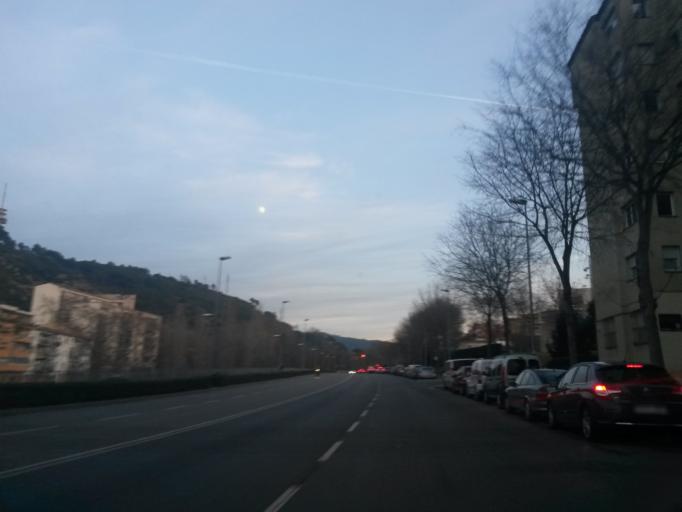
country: ES
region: Catalonia
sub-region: Provincia de Girona
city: Girona
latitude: 41.9734
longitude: 2.8280
